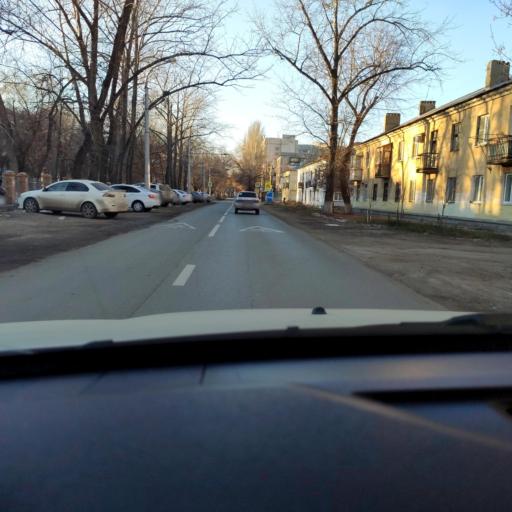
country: RU
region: Samara
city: Samara
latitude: 53.1193
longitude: 50.0818
